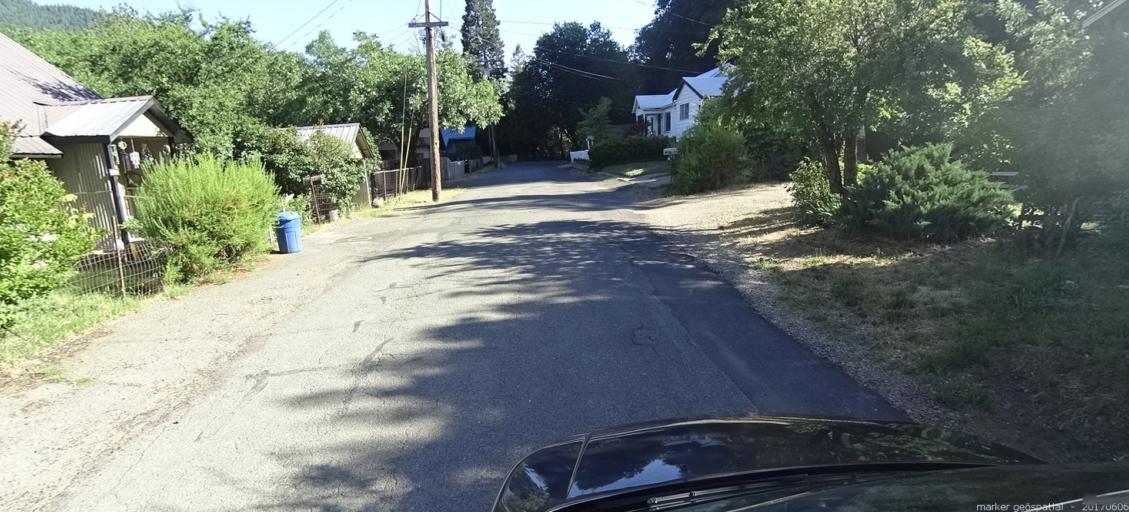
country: US
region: California
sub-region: Siskiyou County
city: Dunsmuir
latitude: 41.2022
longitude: -122.2717
